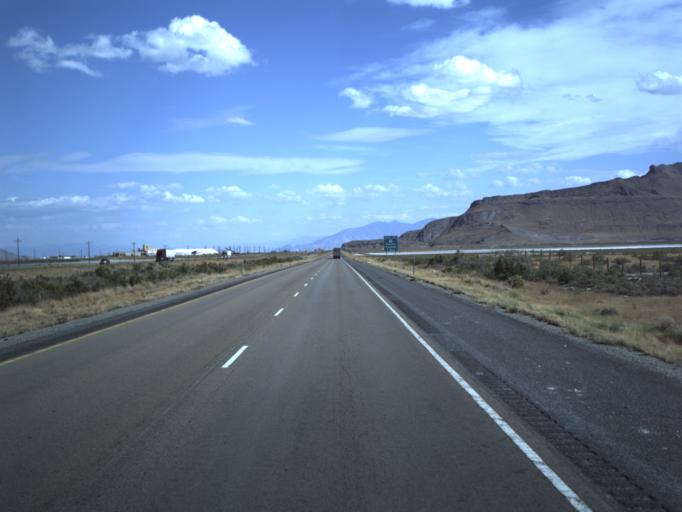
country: US
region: Utah
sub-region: Tooele County
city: Grantsville
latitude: 40.7489
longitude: -112.6860
